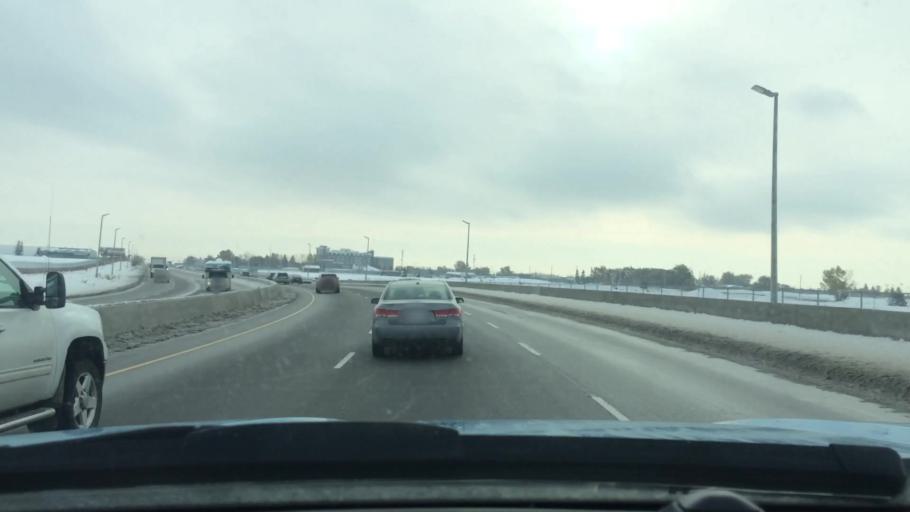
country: CA
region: Alberta
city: Calgary
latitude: 51.0930
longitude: -114.0241
